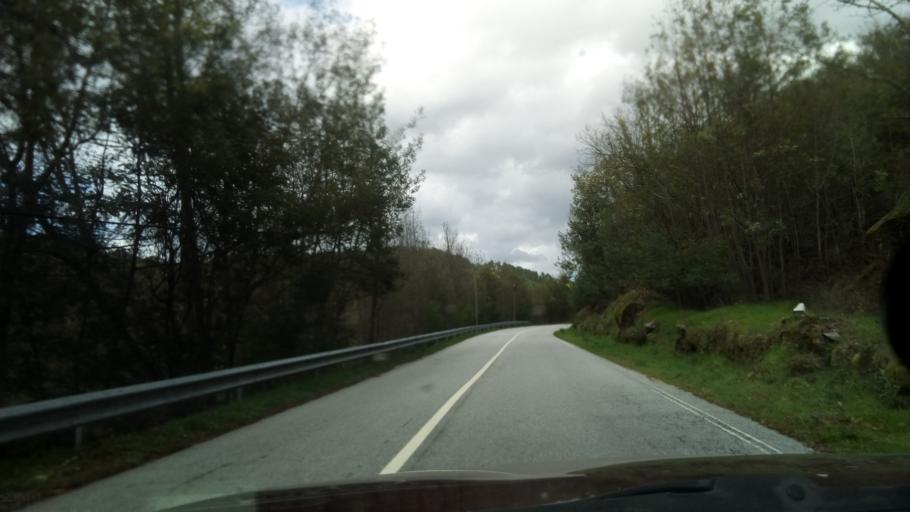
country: PT
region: Guarda
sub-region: Fornos de Algodres
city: Fornos de Algodres
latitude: 40.6159
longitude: -7.5018
